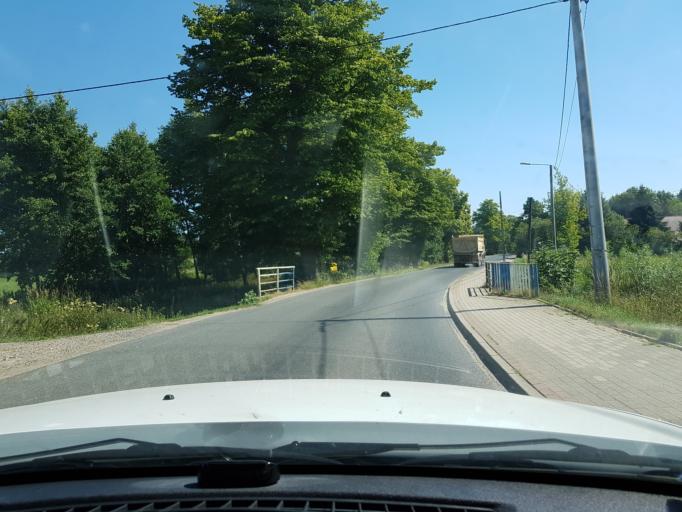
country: PL
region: West Pomeranian Voivodeship
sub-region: Powiat koszalinski
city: Mielno
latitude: 54.2022
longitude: 16.0526
